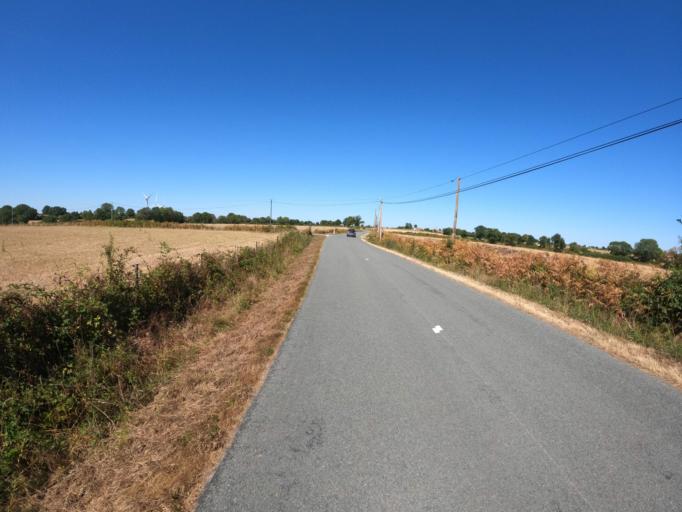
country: FR
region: Pays de la Loire
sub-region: Departement de la Vendee
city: Saint-Aubin-des-Ormeaux
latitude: 47.0114
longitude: -0.9999
